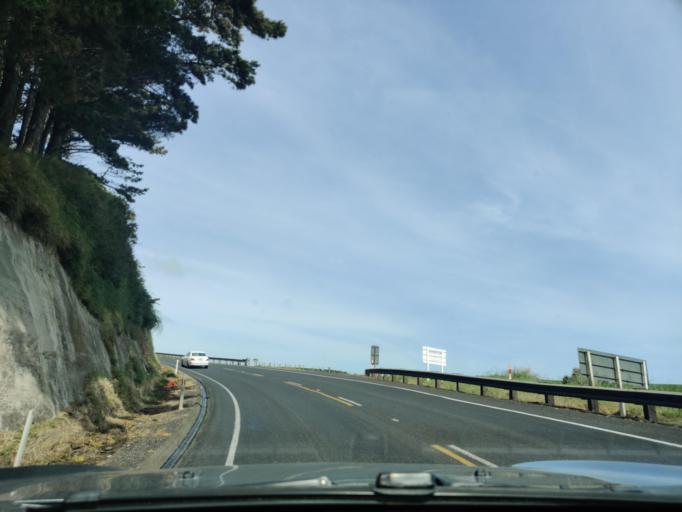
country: NZ
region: Taranaki
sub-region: South Taranaki District
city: Hawera
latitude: -39.6453
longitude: 174.3760
